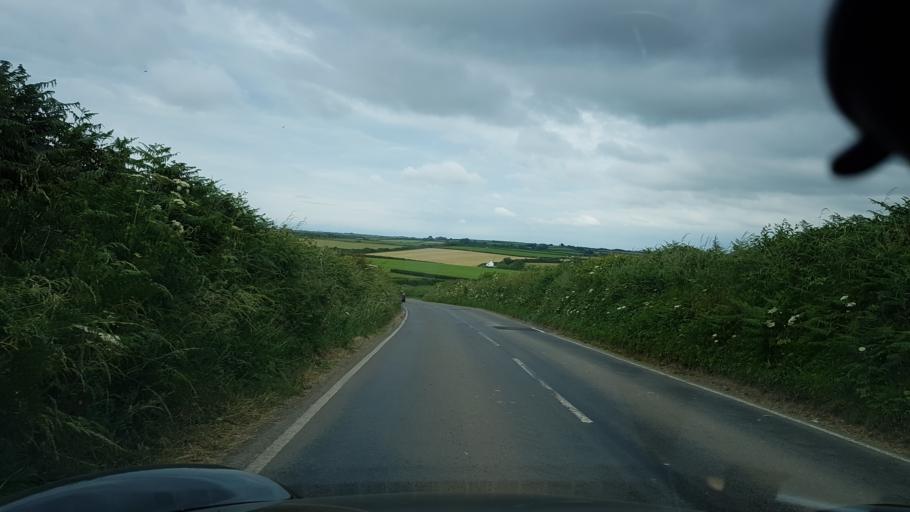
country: GB
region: Wales
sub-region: Pembrokeshire
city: Herbrandston
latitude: 51.7619
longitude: -5.0986
